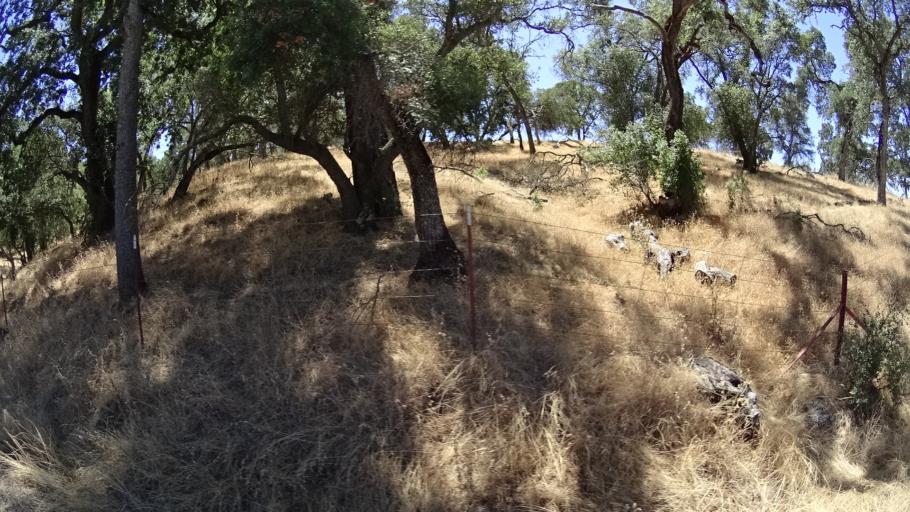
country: US
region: California
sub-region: Calaveras County
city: Valley Springs
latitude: 38.2294
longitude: -120.8480
